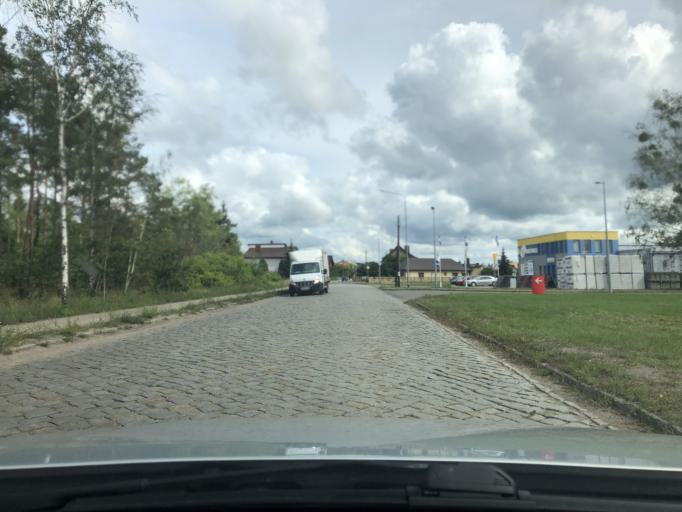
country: PL
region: Greater Poland Voivodeship
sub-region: Powiat czarnkowsko-trzcianecki
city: Krzyz Wielkopolski
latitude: 52.8776
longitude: 15.9966
